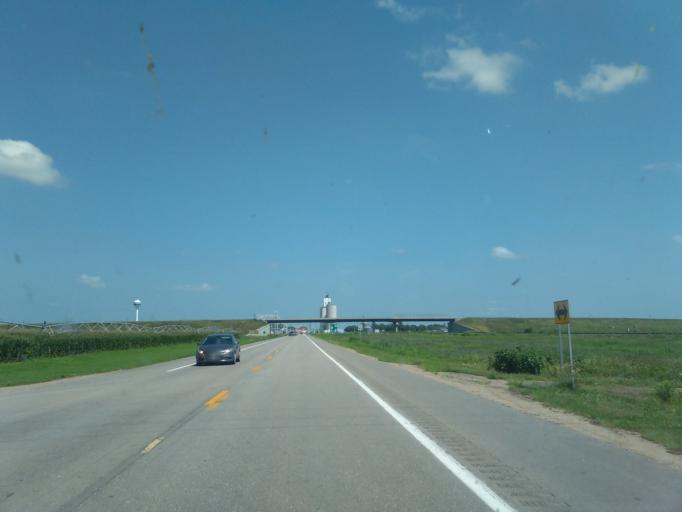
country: US
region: Nebraska
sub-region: Phelps County
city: Holdrege
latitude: 40.7197
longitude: -99.3892
